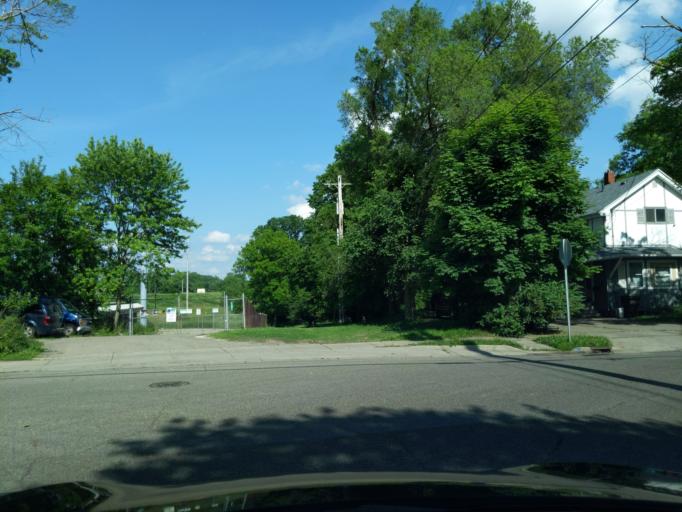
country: US
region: Michigan
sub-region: Ingham County
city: Lansing
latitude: 42.7554
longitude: -84.5348
